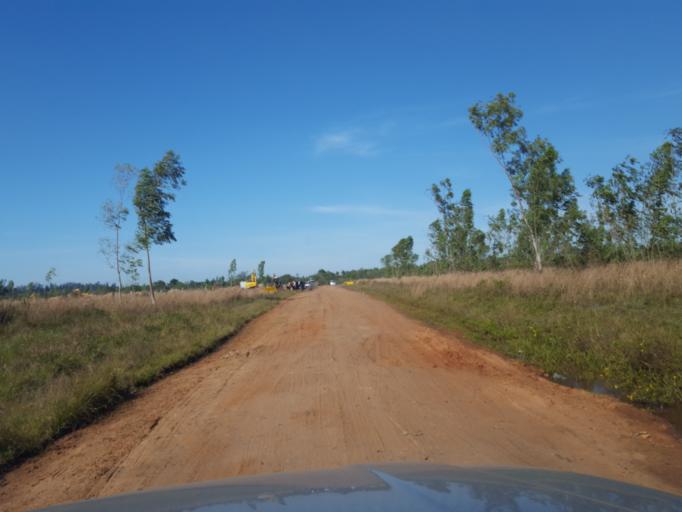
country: PY
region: Cordillera
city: Tobati
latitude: -25.2512
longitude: -57.1149
